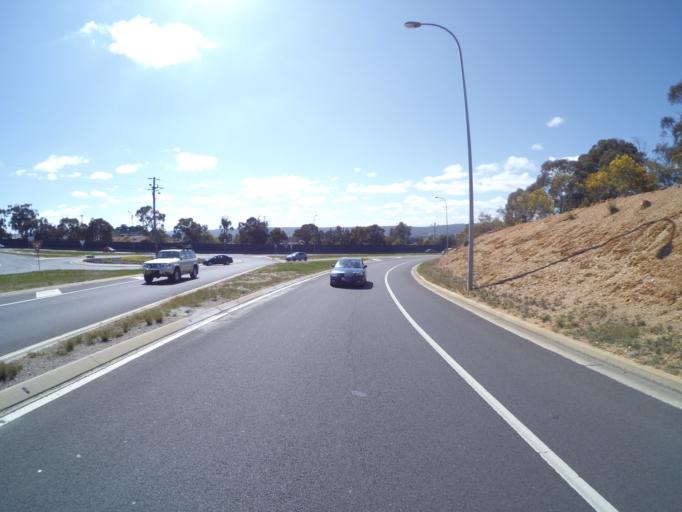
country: AU
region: New South Wales
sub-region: Queanbeyan
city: Queanbeyan
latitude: -35.3563
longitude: 149.2154
